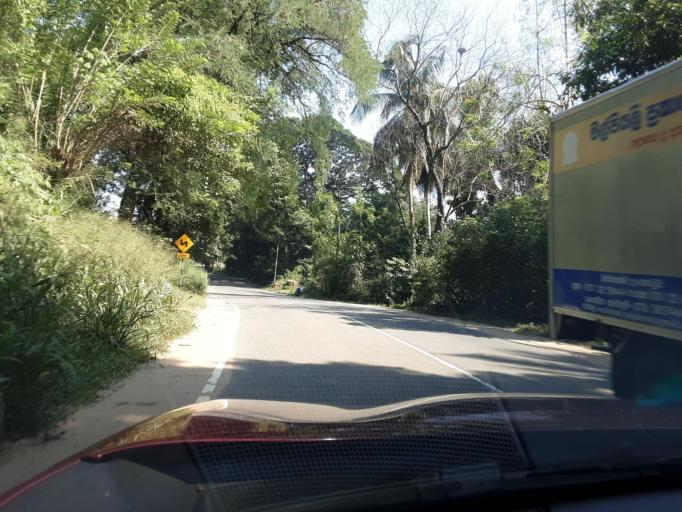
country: LK
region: Uva
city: Badulla
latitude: 7.1626
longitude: 81.0518
